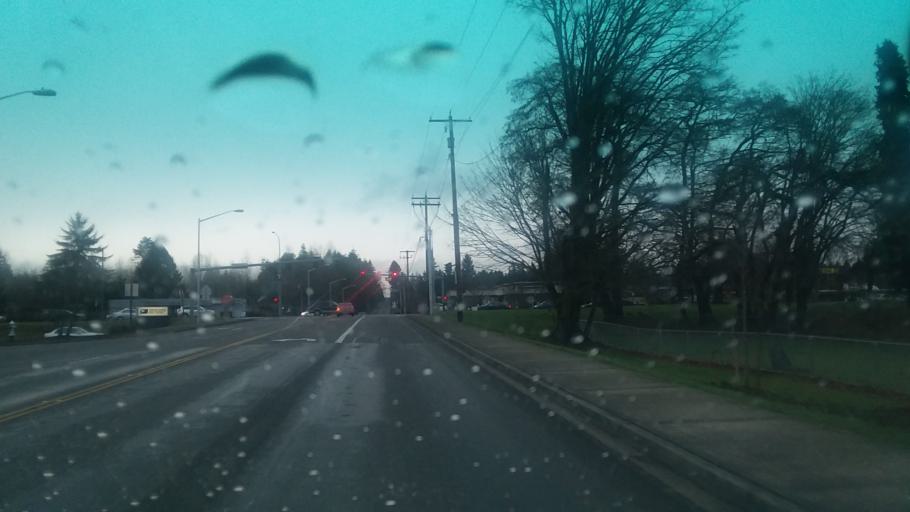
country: US
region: Washington
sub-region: Pierce County
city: South Hill
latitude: 47.1330
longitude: -122.2944
